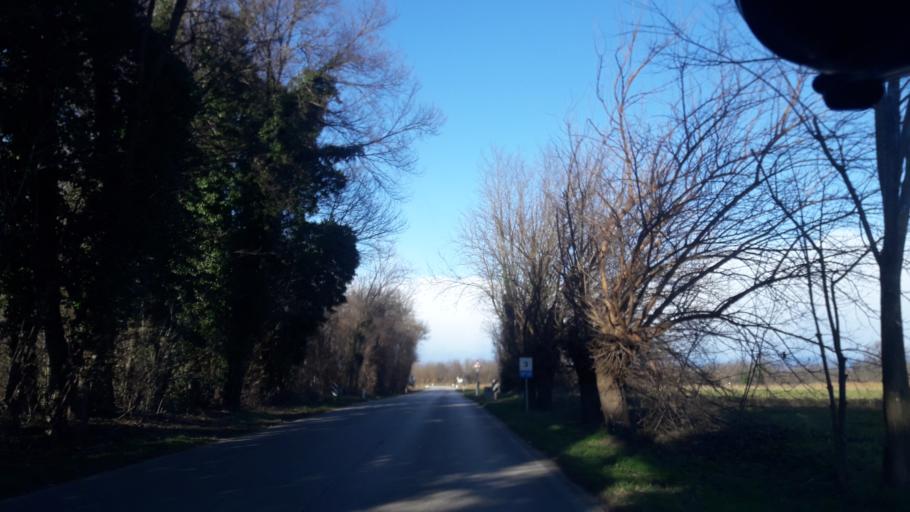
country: IT
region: Friuli Venezia Giulia
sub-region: Provincia di Udine
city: Bressa
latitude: 46.0414
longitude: 13.1439
